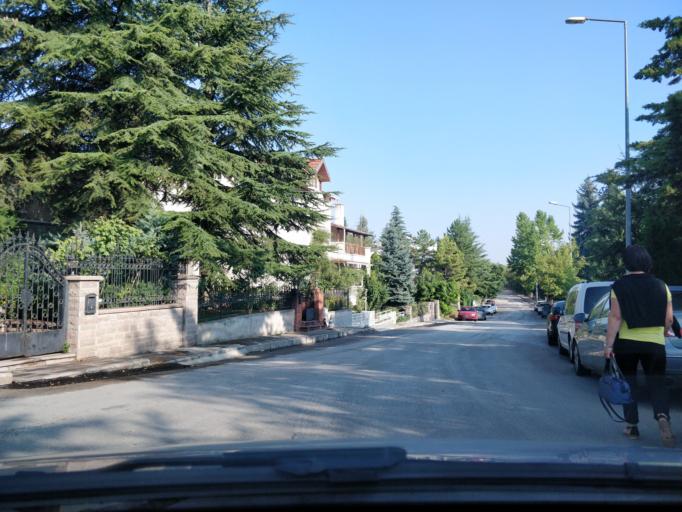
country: TR
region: Ankara
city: Batikent
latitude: 39.8949
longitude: 32.7267
